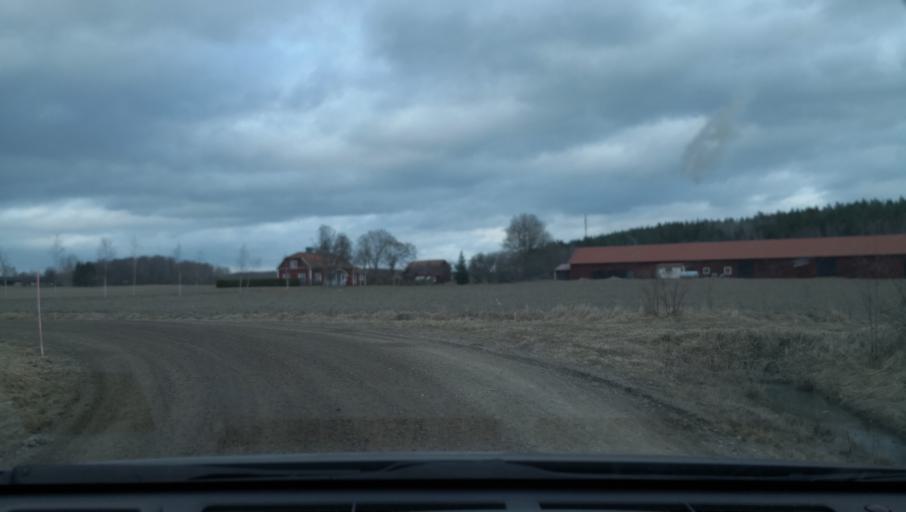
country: SE
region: Vaestmanland
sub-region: Kopings Kommun
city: Kolsva
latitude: 59.5354
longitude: 15.8946
